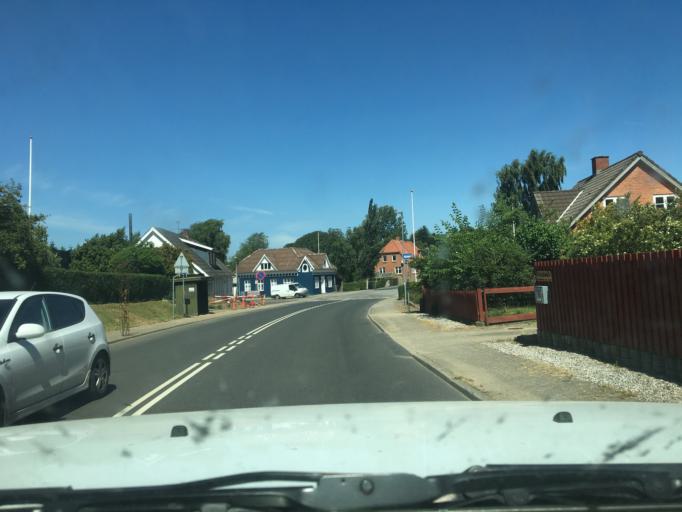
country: DK
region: Central Jutland
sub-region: Favrskov Kommune
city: Ulstrup
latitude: 56.4100
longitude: 9.7904
